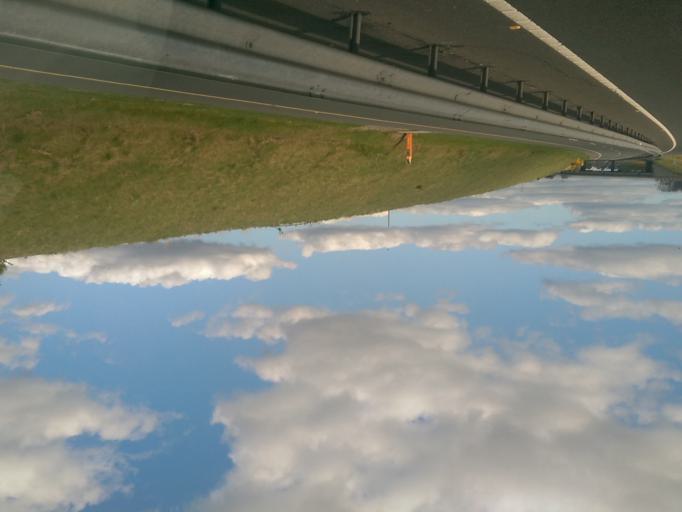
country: IE
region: Leinster
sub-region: An Iarmhi
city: Athlone
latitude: 53.3618
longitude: -8.0629
